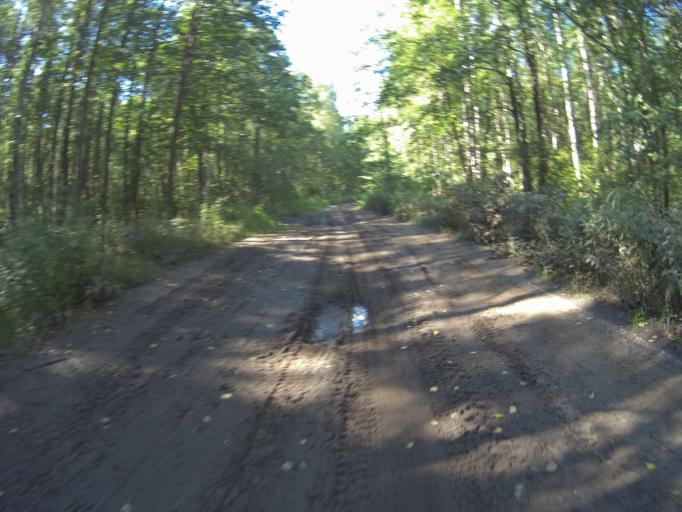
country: RU
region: Vladimir
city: Raduzhnyy
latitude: 55.9279
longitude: 40.2427
